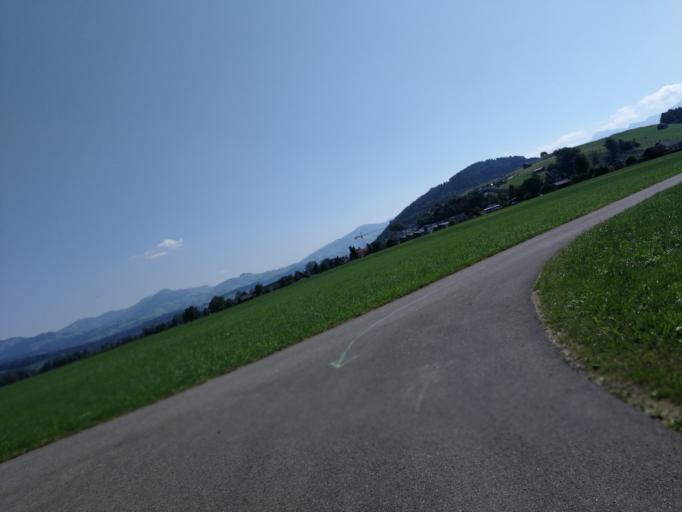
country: CH
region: Schwyz
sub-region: Bezirk March
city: Lachen
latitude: 47.1989
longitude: 8.8756
